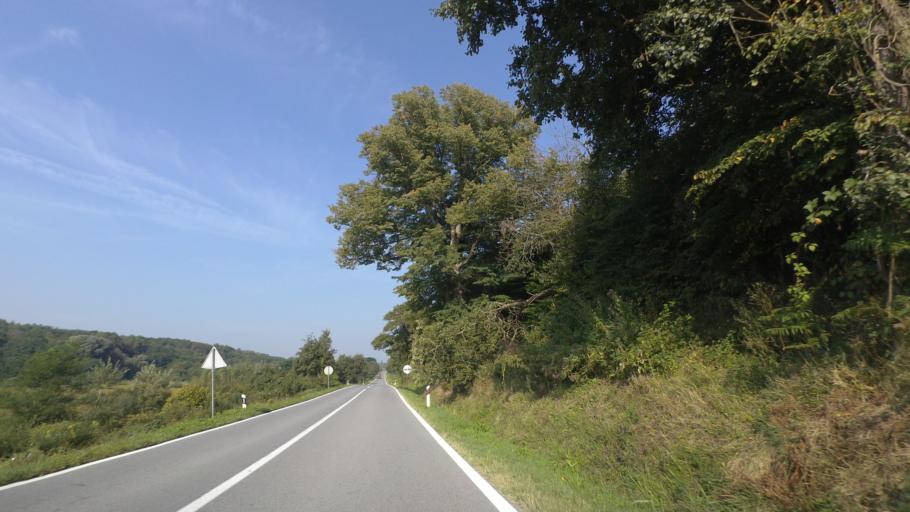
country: HR
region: Bjelovarsko-Bilogorska
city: Sirac
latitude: 45.4723
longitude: 17.3215
